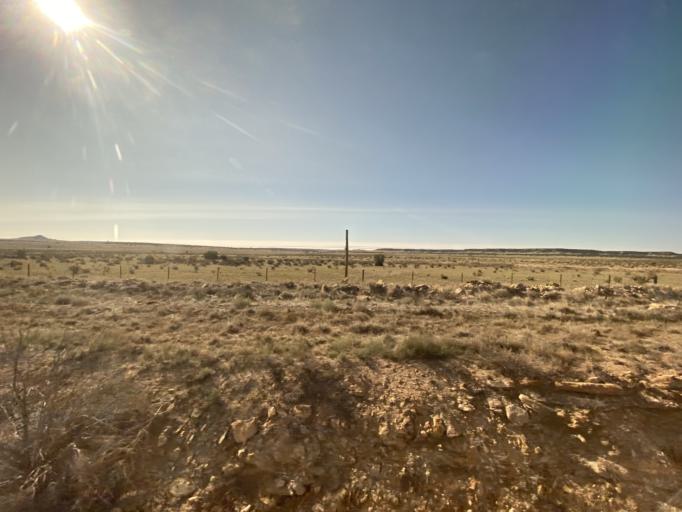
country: US
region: Colorado
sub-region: Otero County
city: Fowler
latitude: 37.5692
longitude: -104.0653
